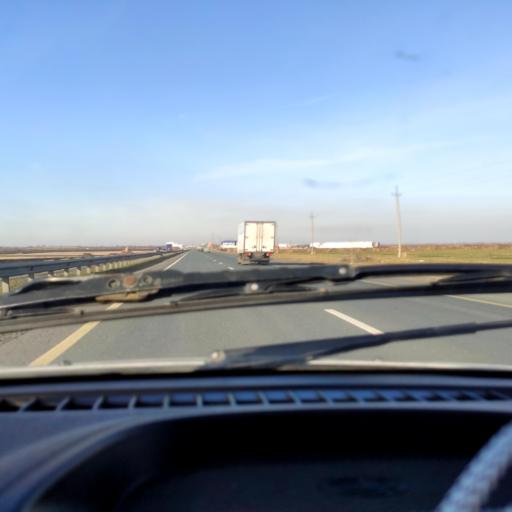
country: RU
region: Samara
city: Zhigulevsk
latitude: 53.5504
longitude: 49.5076
